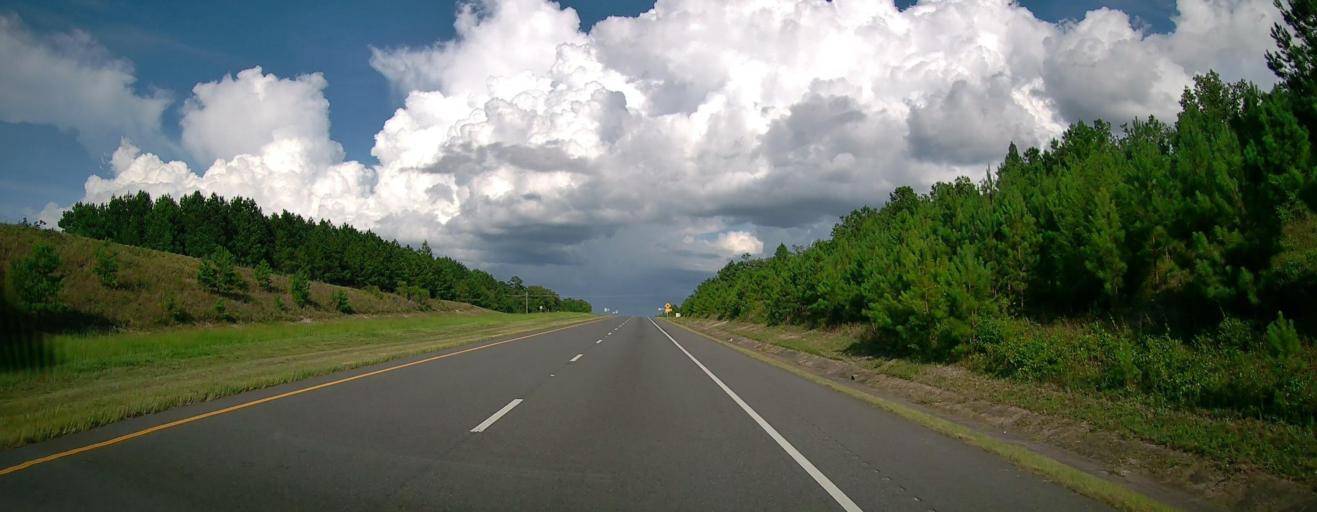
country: US
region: Georgia
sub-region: Talbot County
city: Talbotton
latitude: 32.5971
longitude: -84.4655
